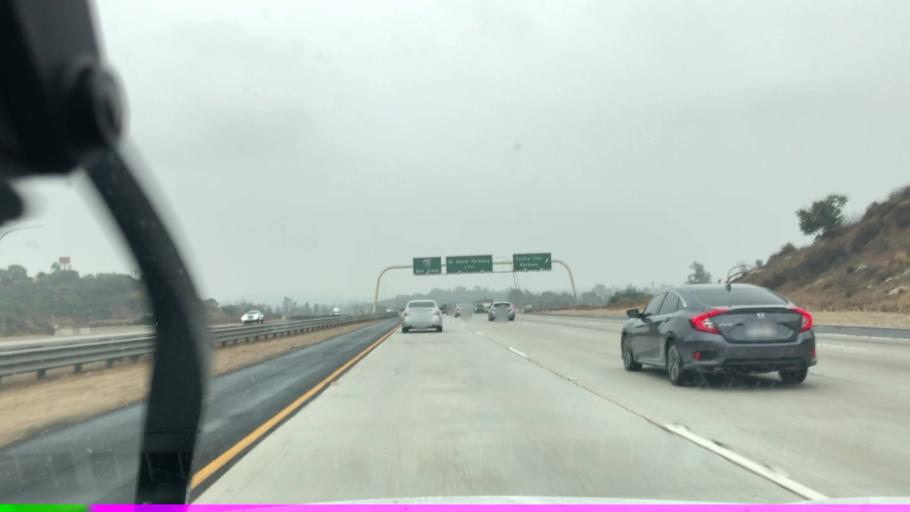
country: US
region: California
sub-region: San Diego County
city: Escondido
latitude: 33.1670
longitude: -117.1086
